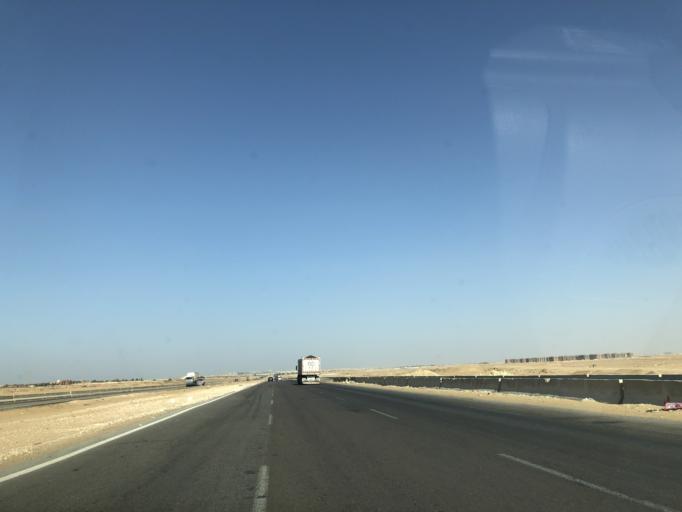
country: EG
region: Muhafazat al Minufiyah
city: Ashmun
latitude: 30.0676
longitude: 30.8701
